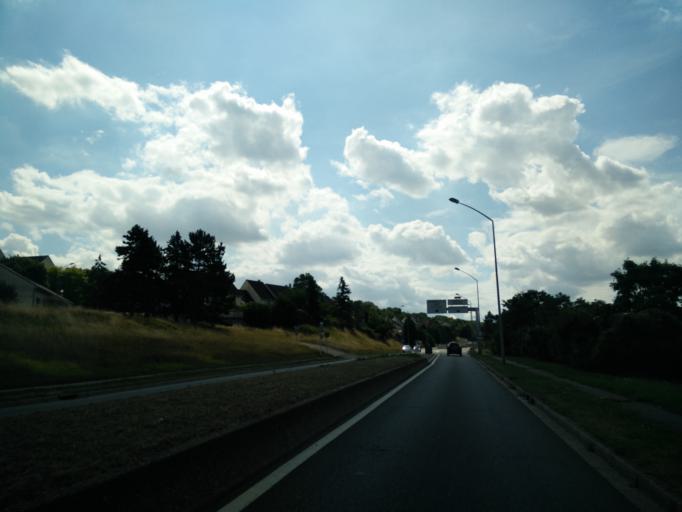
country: FR
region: Ile-de-France
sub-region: Departement des Yvelines
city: Mantes-la-Ville
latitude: 48.9671
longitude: 1.7170
